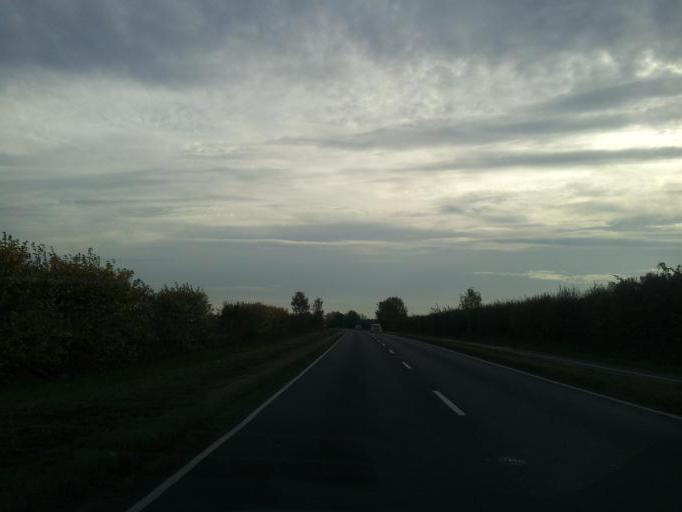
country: GB
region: England
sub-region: Cambridgeshire
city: Duxford
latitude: 52.0959
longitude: 0.1801
